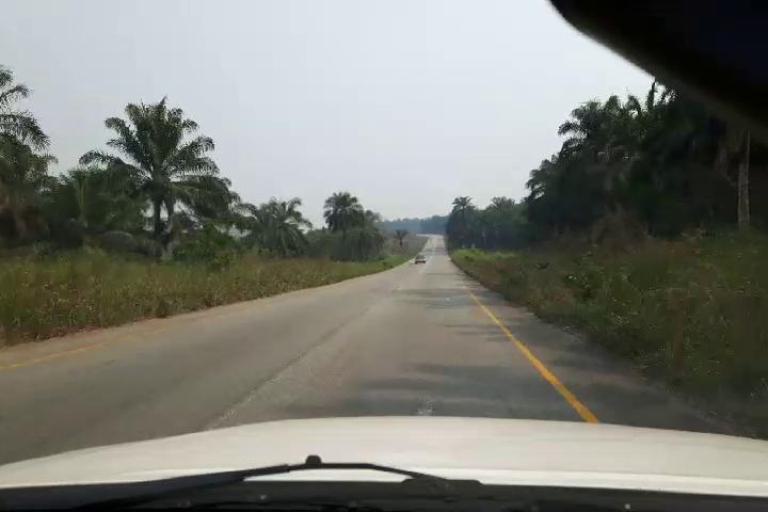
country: SL
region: Southern Province
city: Largo
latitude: 8.2180
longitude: -12.0749
